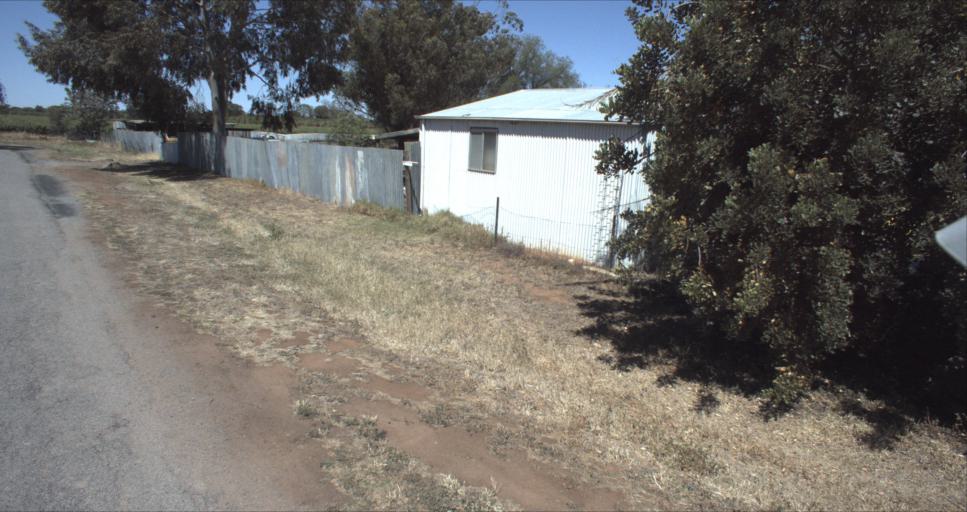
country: AU
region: New South Wales
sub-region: Leeton
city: Leeton
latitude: -34.5239
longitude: 146.3342
